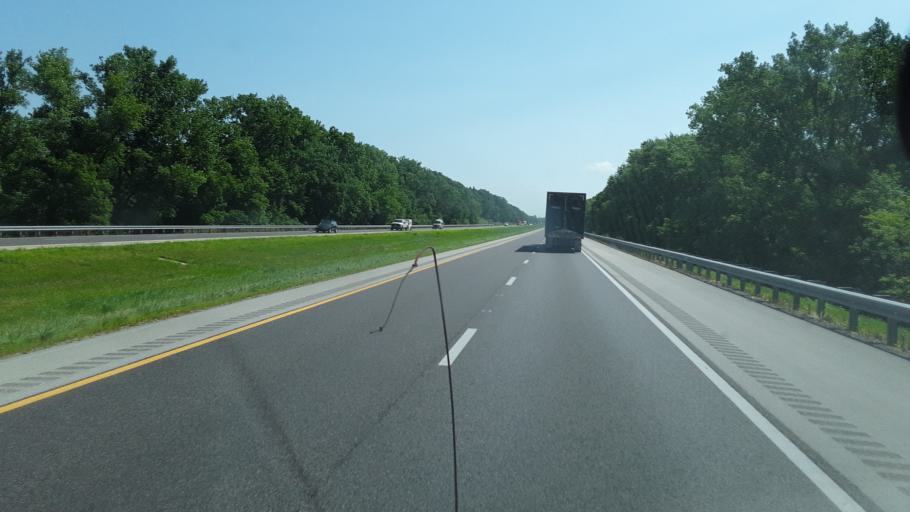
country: US
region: Illinois
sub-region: Cumberland County
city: Toledo
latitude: 39.2056
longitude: -88.2824
